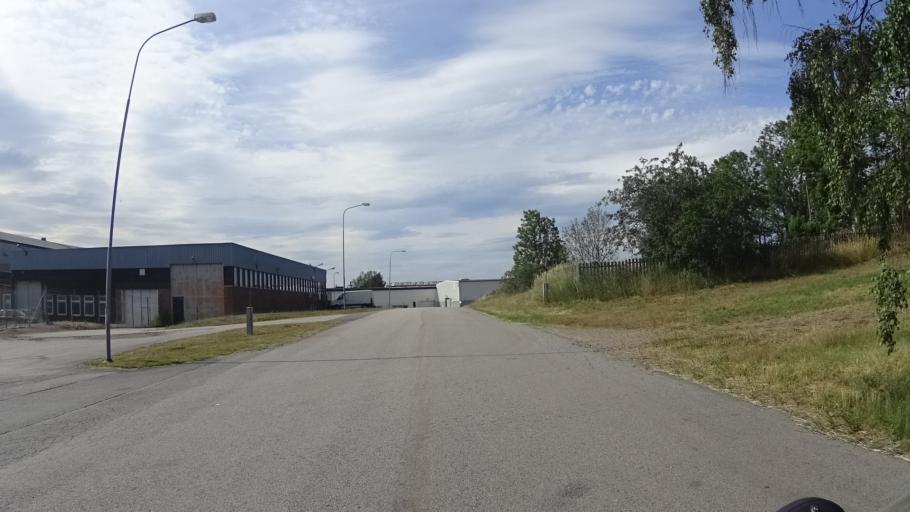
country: SE
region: Kalmar
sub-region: Vasterviks Kommun
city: Gamleby
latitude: 57.8870
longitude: 16.4120
